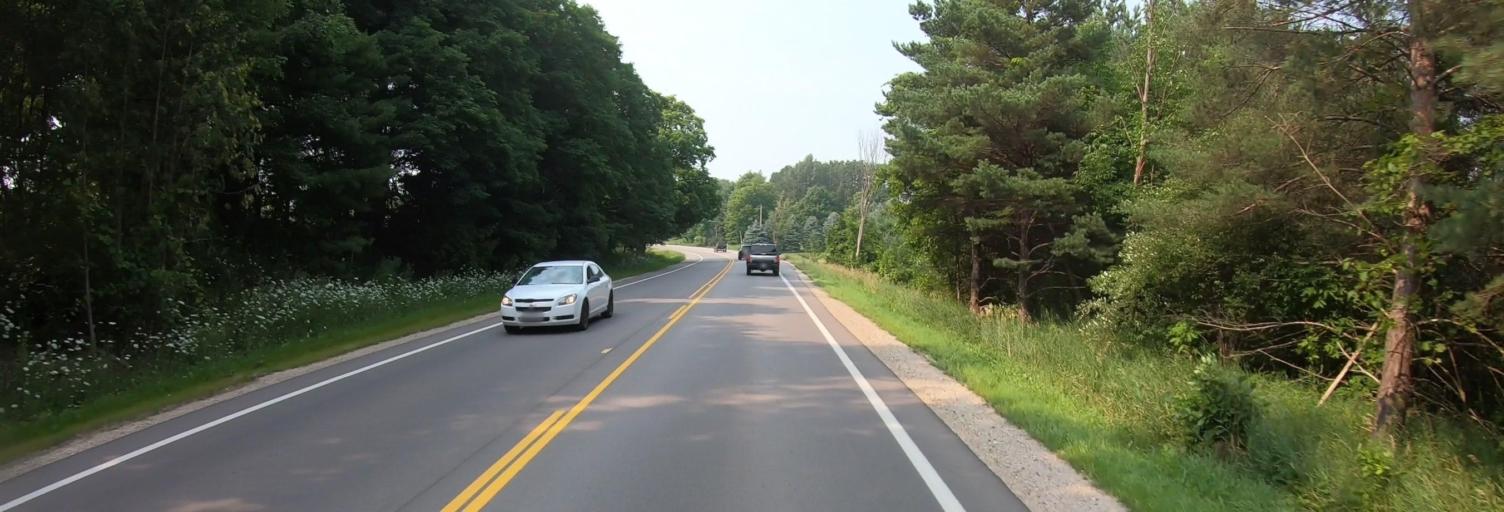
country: US
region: Michigan
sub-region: Charlevoix County
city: Charlevoix
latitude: 45.2538
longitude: -85.2613
